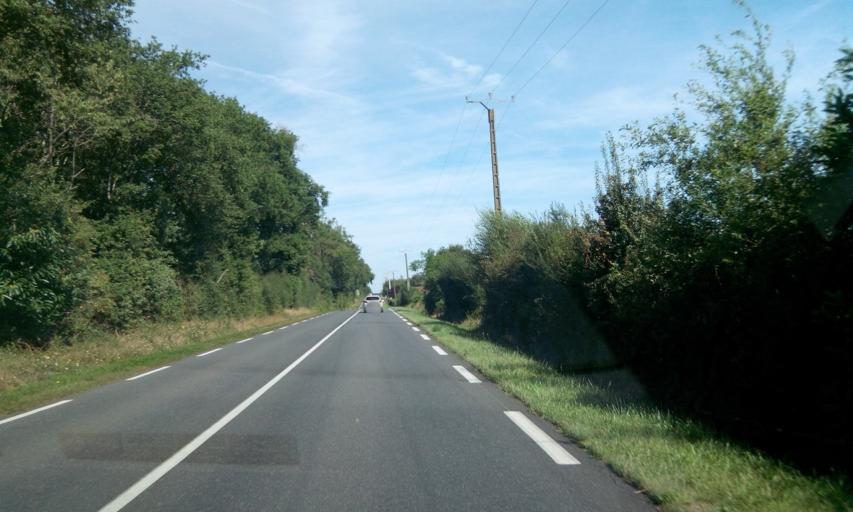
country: FR
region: Poitou-Charentes
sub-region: Departement de la Vienne
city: Availles-Limouzine
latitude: 46.0942
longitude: 0.5838
